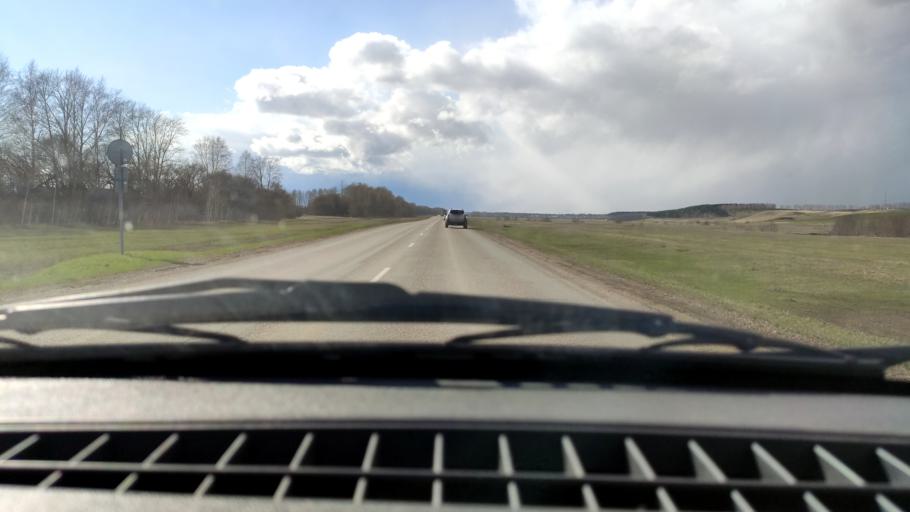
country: RU
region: Bashkortostan
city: Chekmagush
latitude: 55.1227
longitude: 54.7246
